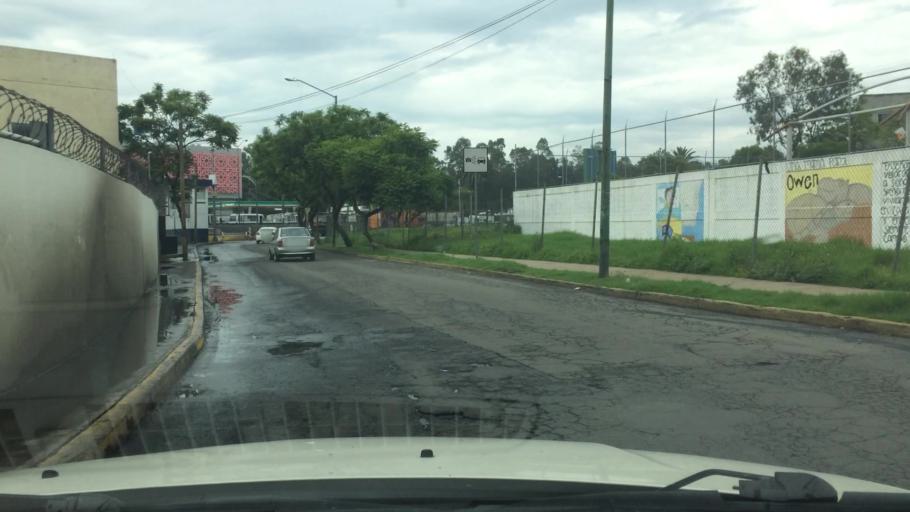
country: MX
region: Mexico City
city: Xochimilco
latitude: 19.2959
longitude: -99.1024
